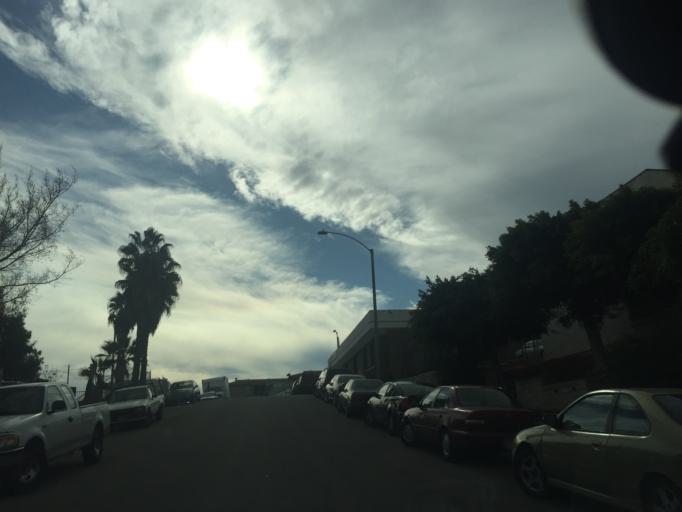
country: US
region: California
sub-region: San Diego County
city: Lemon Grove
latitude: 32.7504
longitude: -117.0901
